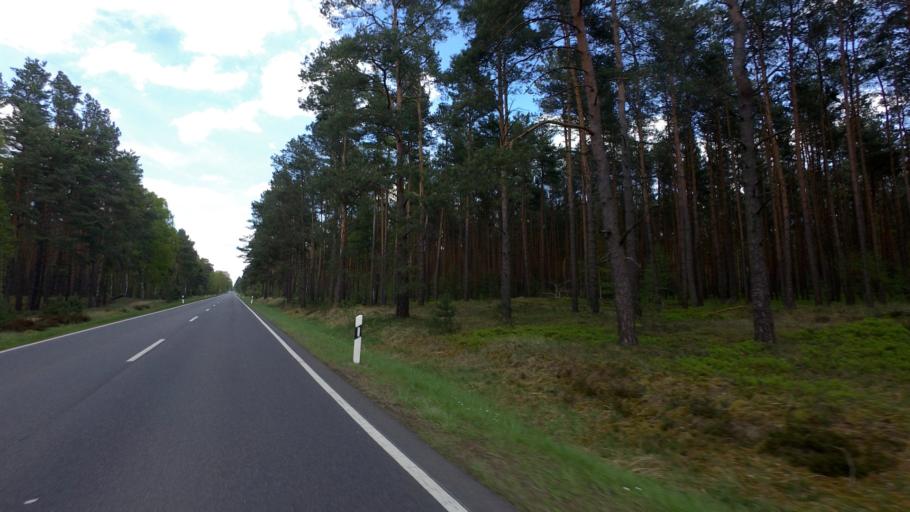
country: DE
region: Brandenburg
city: Marienwerder
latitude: 52.9591
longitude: 13.5684
